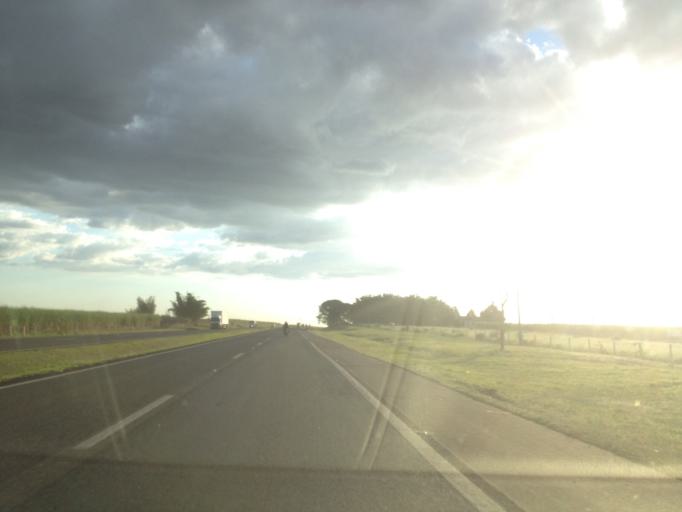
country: BR
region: Sao Paulo
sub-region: Jau
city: Jau
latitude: -22.2701
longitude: -48.4652
